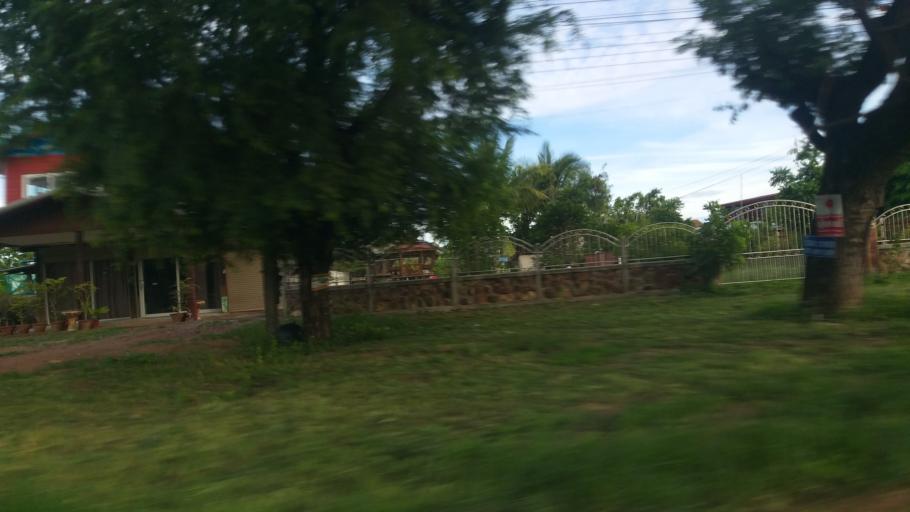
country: TH
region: Chaiyaphum
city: Phu Khiao
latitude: 16.3409
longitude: 102.2363
